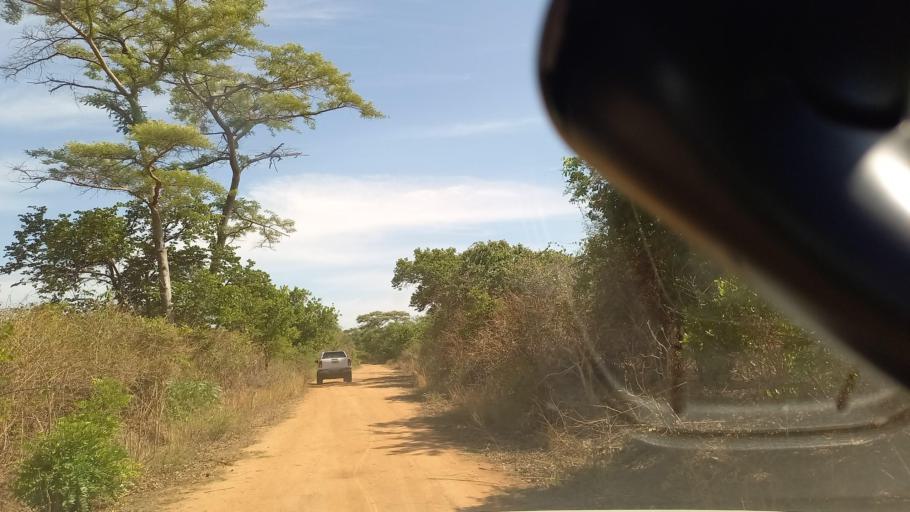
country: ZM
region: Southern
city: Mazabuka
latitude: -16.0406
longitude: 27.6216
